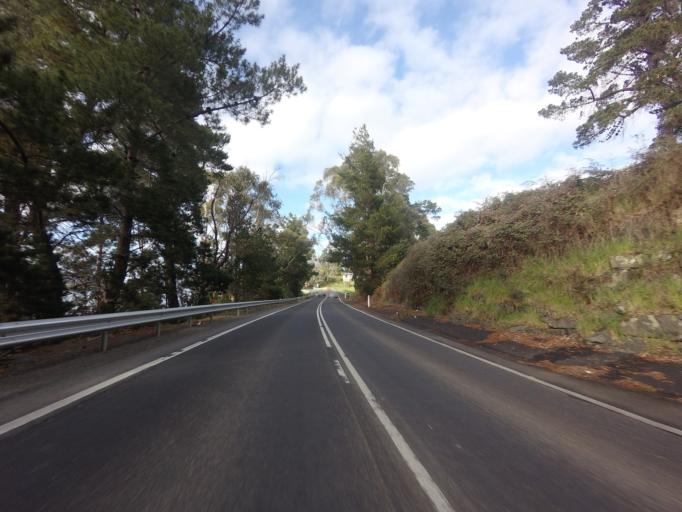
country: AU
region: Tasmania
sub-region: Huon Valley
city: Geeveston
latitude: -43.1530
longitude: 146.9809
